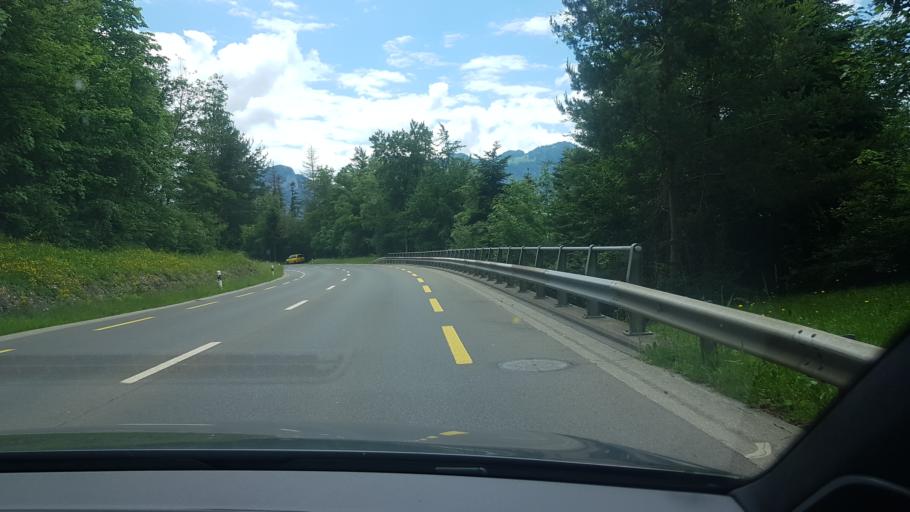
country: CH
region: Schwyz
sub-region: Bezirk Schwyz
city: Steinen
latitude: 47.0593
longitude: 8.6210
